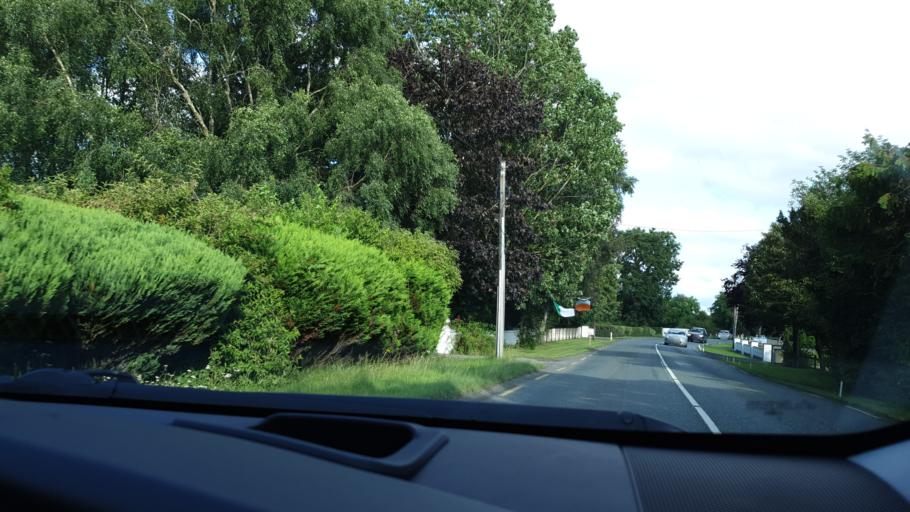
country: IE
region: Leinster
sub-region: An Mhi
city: Ashbourne
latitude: 53.4965
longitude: -6.4012
